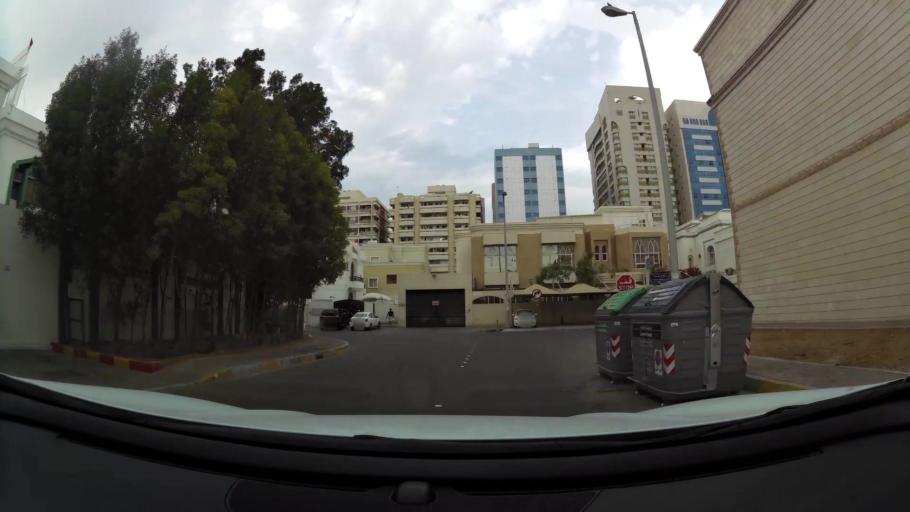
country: AE
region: Abu Dhabi
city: Abu Dhabi
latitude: 24.4790
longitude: 54.3730
